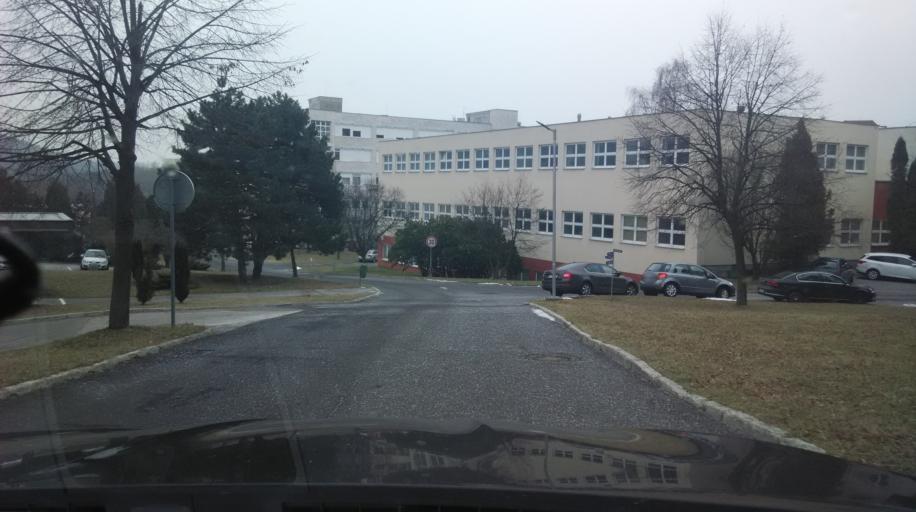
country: AT
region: Lower Austria
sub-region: Politischer Bezirk Bruck an der Leitha
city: Wolfsthal
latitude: 48.1684
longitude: 17.0450
